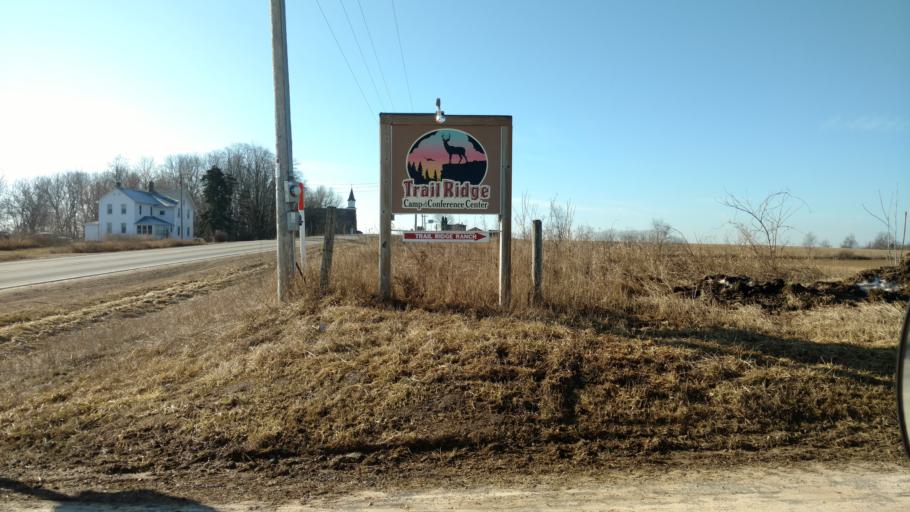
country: US
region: Wisconsin
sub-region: Vernon County
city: Hillsboro
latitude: 43.6258
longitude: -90.4524
